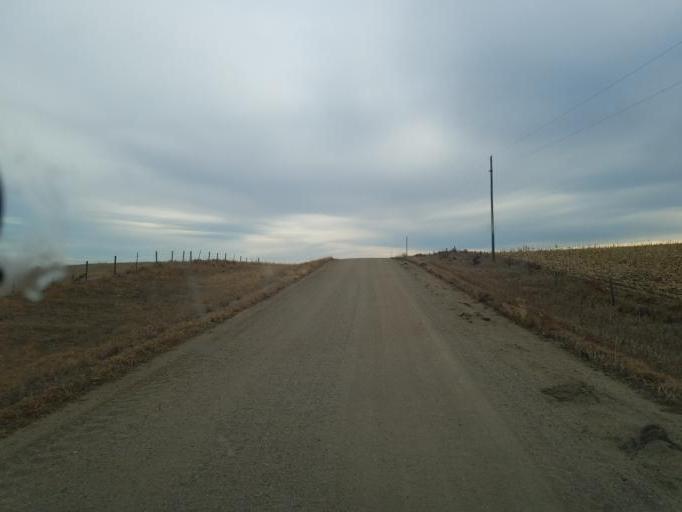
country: US
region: Nebraska
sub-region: Knox County
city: Bloomfield
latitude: 42.5250
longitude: -97.7343
